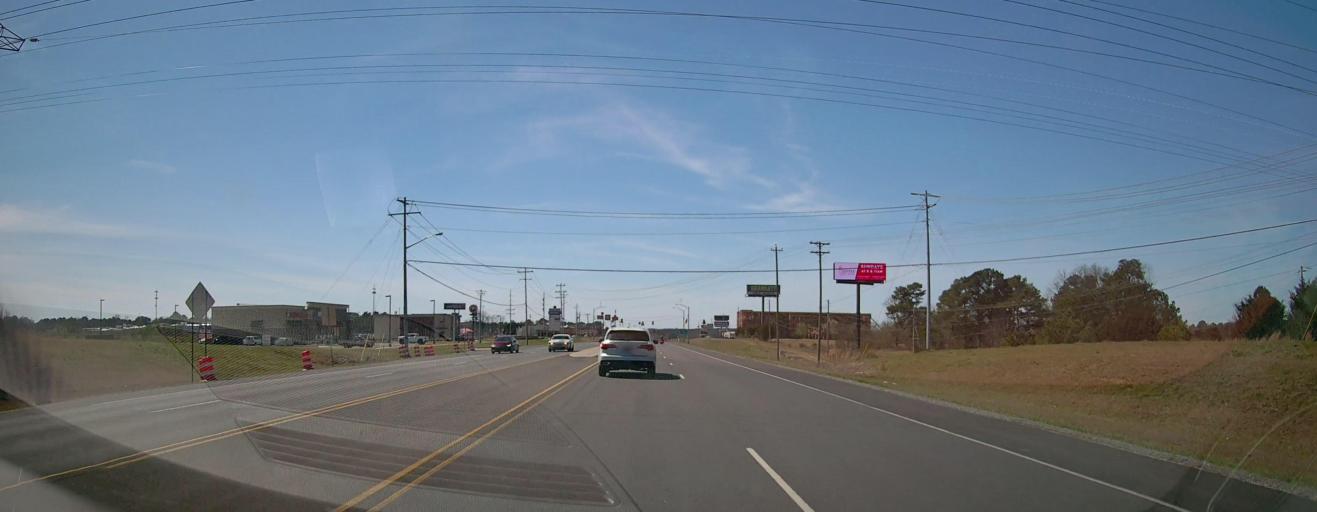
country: US
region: Alabama
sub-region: Cullman County
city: Cullman
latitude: 34.2065
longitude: -86.8653
